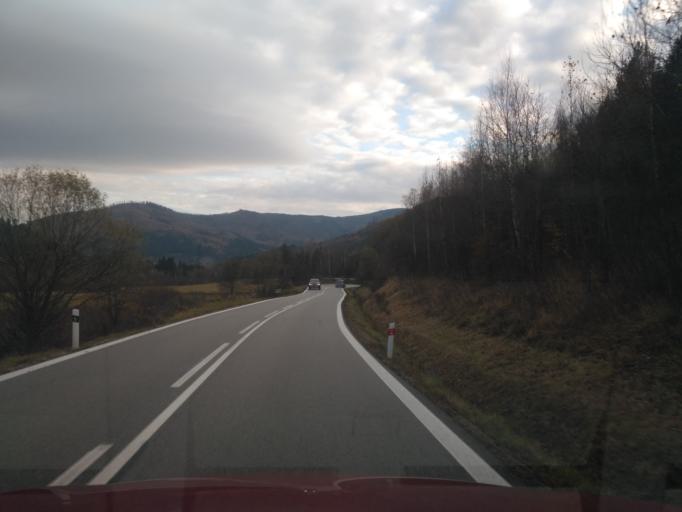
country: SK
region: Kosicky
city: Spisska Nova Ves
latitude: 48.8240
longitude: 20.6565
